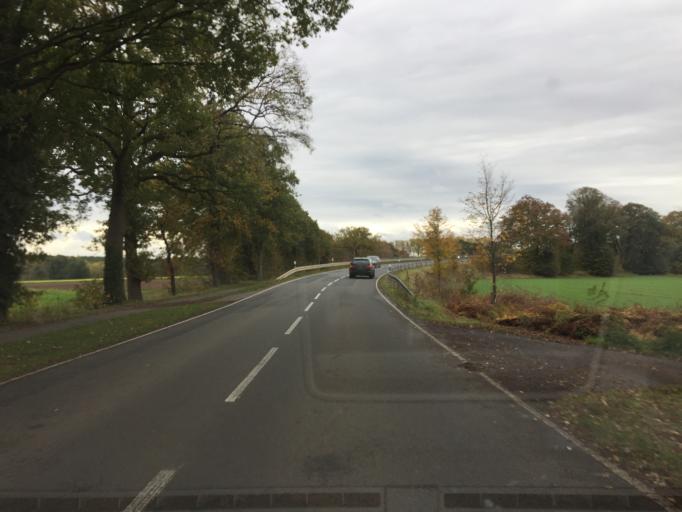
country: DE
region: Lower Saxony
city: Linsburg
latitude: 52.5802
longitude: 9.2950
